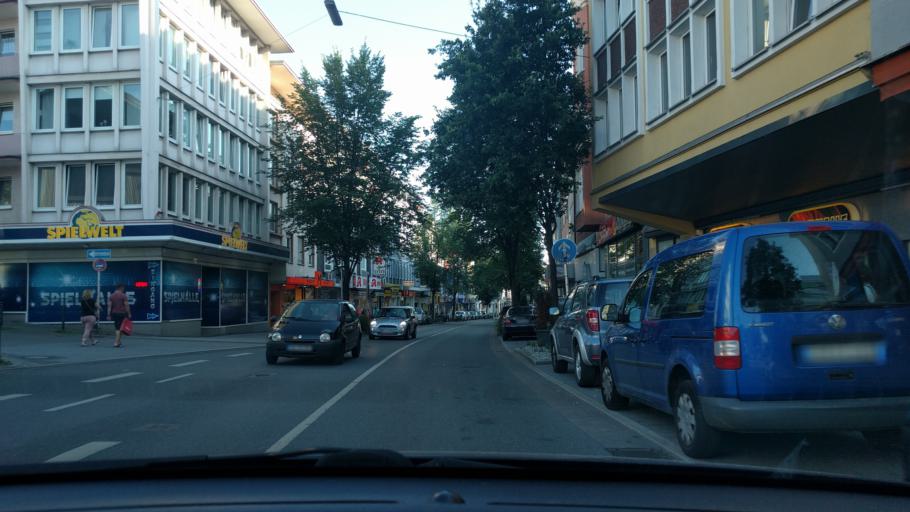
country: DE
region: North Rhine-Westphalia
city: Witten
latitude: 51.4389
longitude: 7.3369
